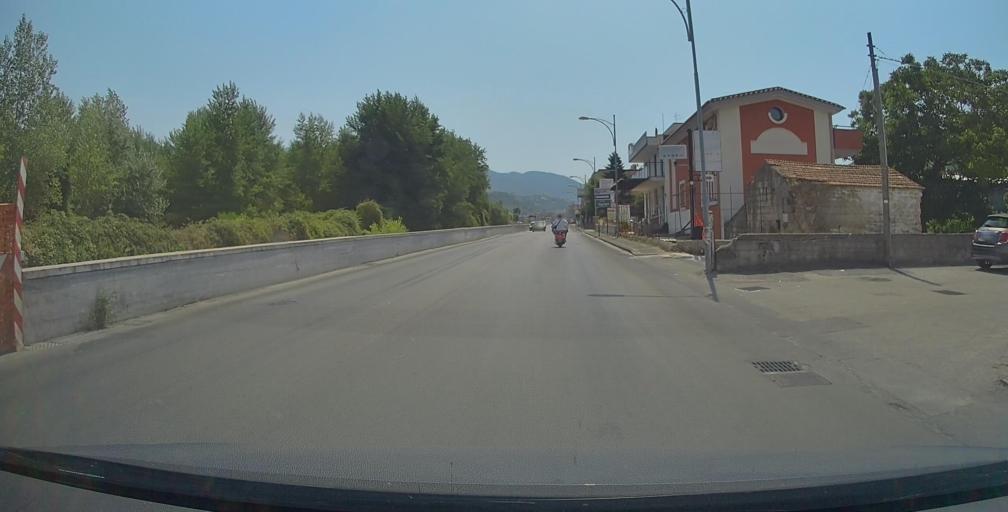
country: IT
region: Campania
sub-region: Provincia di Salerno
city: Nocera Superiore
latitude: 40.7378
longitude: 14.6756
